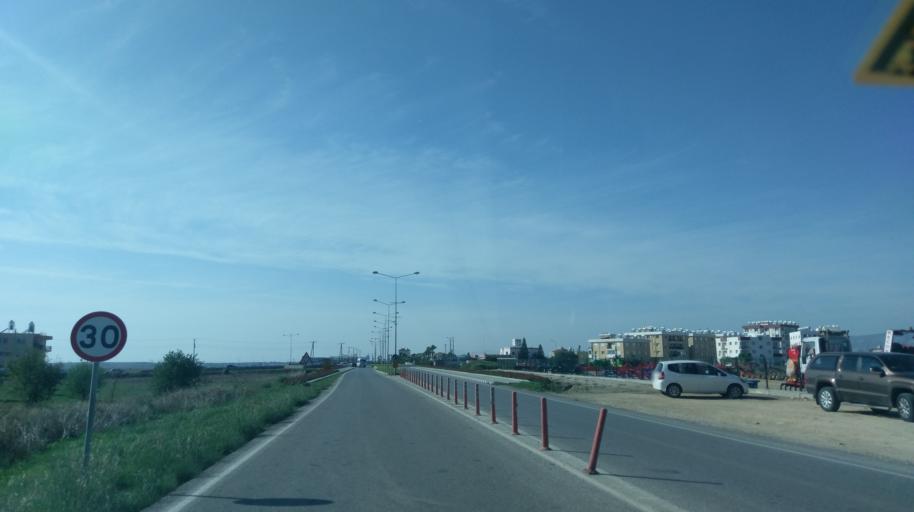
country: CY
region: Ammochostos
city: Trikomo
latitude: 35.2786
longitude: 33.9001
